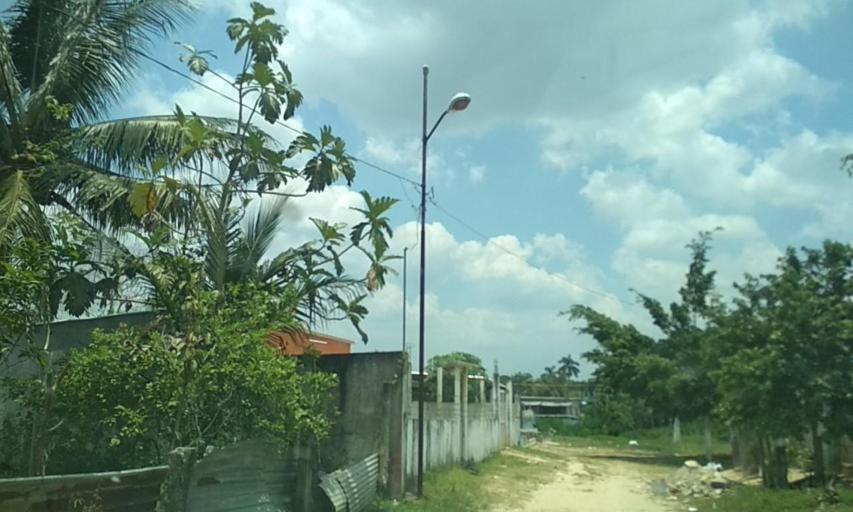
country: MX
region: Veracruz
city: Las Choapas
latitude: 17.9140
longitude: -94.0888
